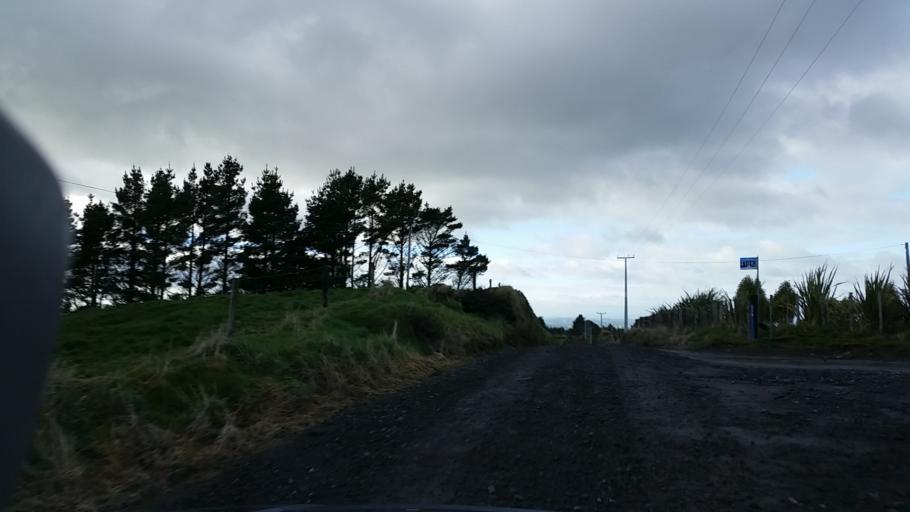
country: NZ
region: Taranaki
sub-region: South Taranaki District
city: Eltham
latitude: -39.3337
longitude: 174.1761
